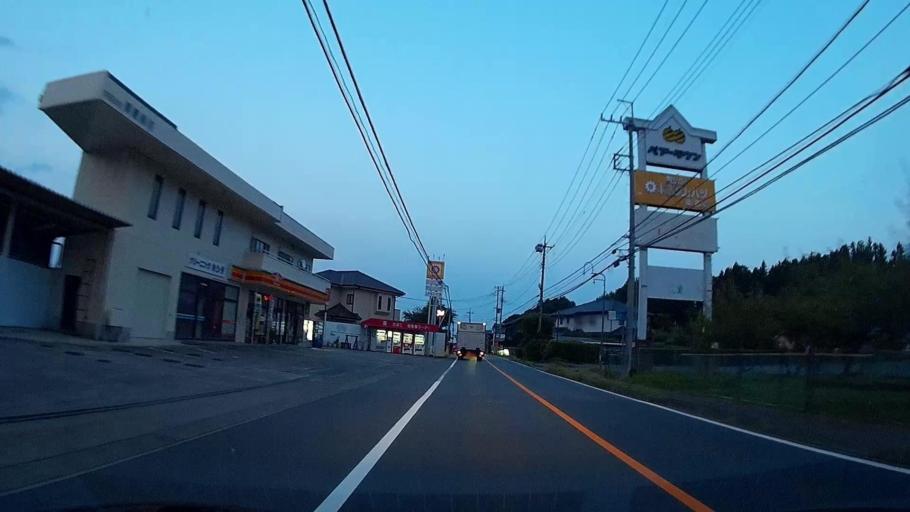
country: JP
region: Gunma
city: Annaka
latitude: 36.3749
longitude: 138.8953
